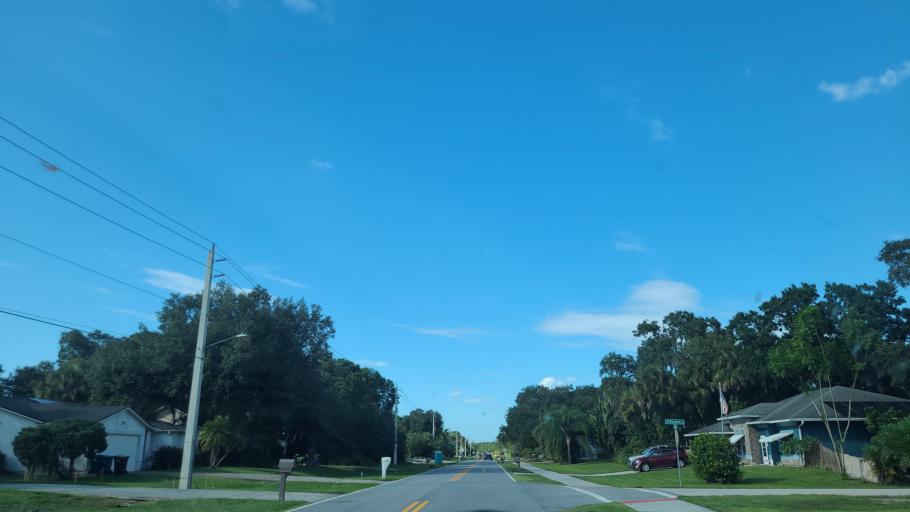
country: US
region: Florida
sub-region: Brevard County
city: Grant-Valkaria
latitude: 27.9641
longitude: -80.6610
